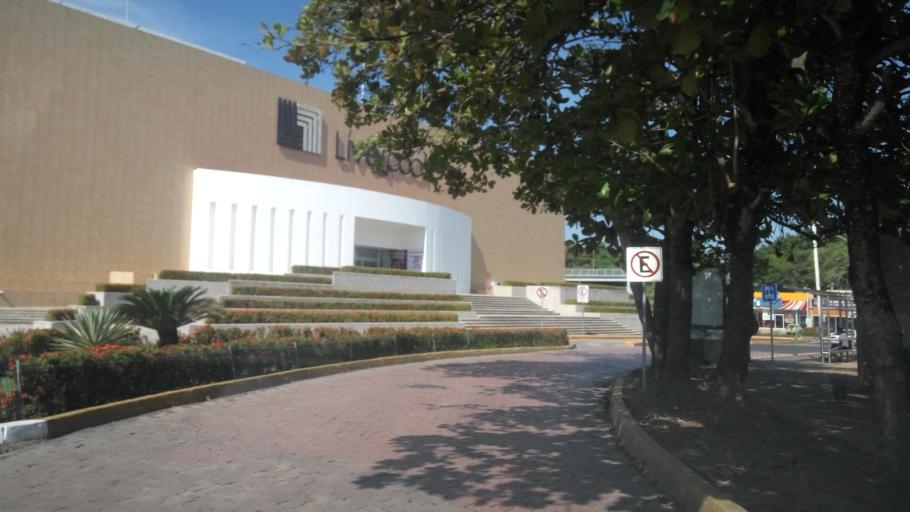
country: MX
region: Tabasco
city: Villahermosa
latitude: 18.0008
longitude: -92.9449
